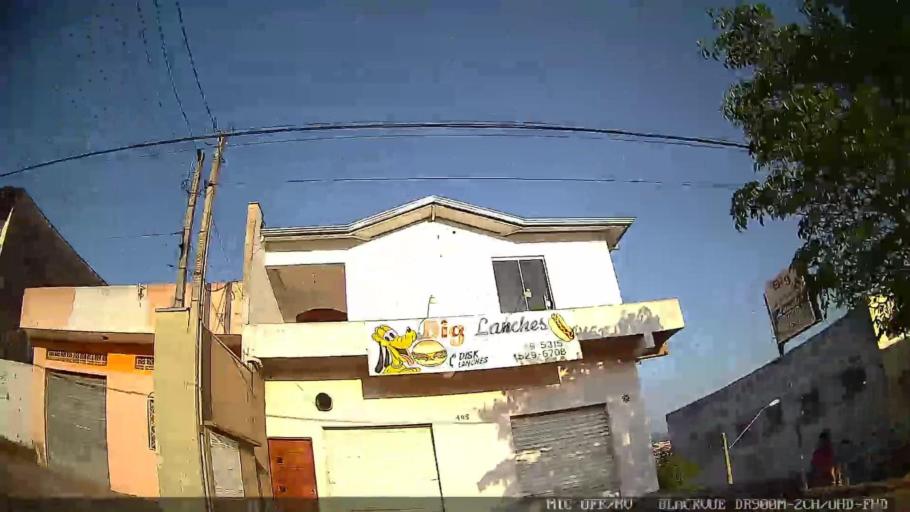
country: BR
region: Sao Paulo
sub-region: Cabreuva
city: Cabreuva
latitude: -23.2593
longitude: -47.0558
